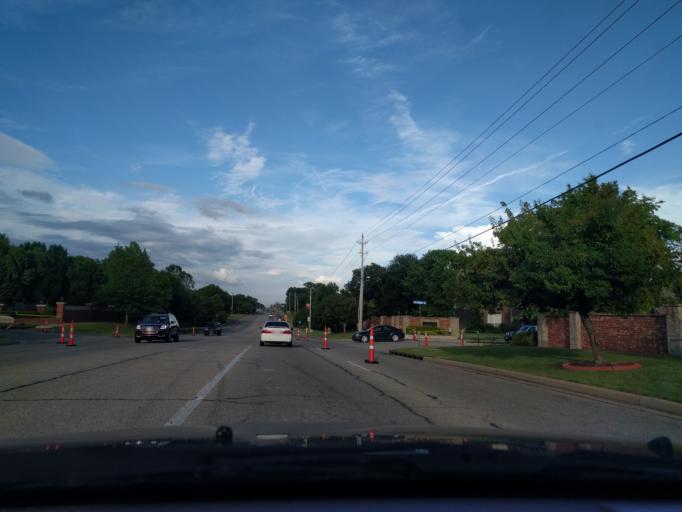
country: US
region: Oklahoma
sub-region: Tulsa County
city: Broken Arrow
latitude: 36.0609
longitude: -95.8409
